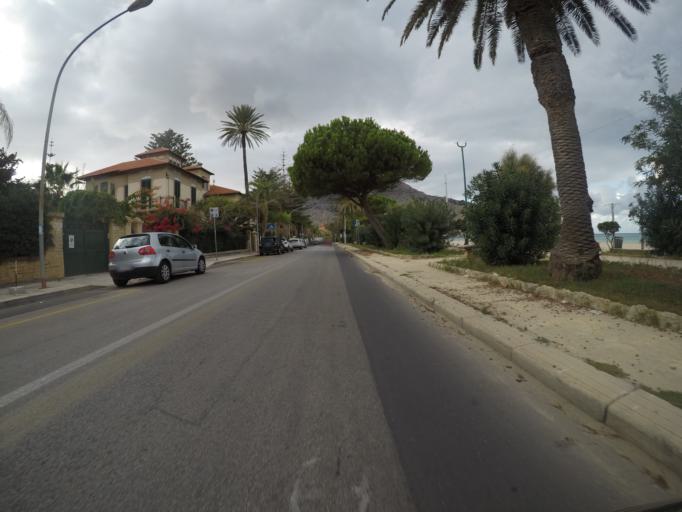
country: IT
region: Sicily
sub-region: Palermo
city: Palermo
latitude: 38.1991
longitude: 13.3290
